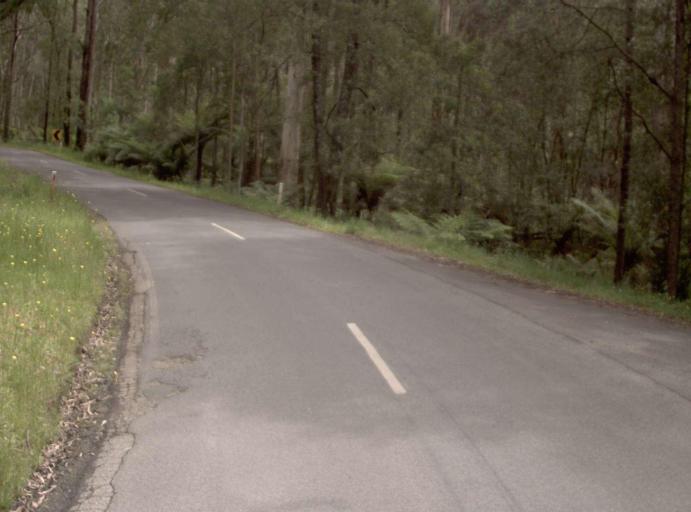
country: AU
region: Victoria
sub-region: Baw Baw
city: Warragul
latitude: -37.8998
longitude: 146.0994
